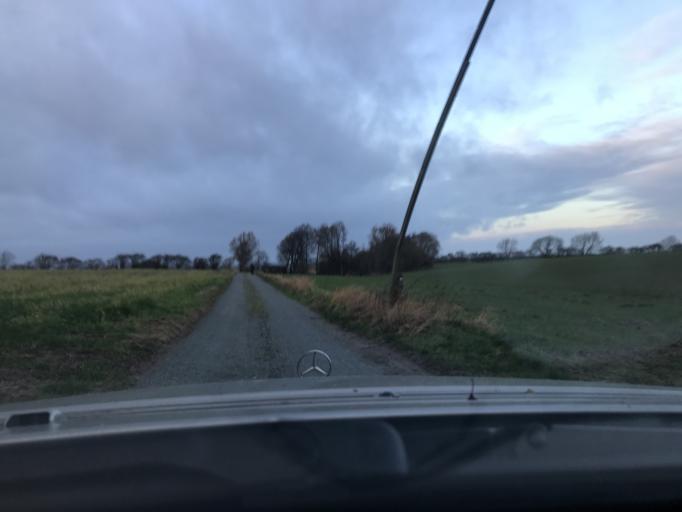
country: DK
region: South Denmark
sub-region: Sonderborg Kommune
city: Nordborg
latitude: 55.0688
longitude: 9.6924
